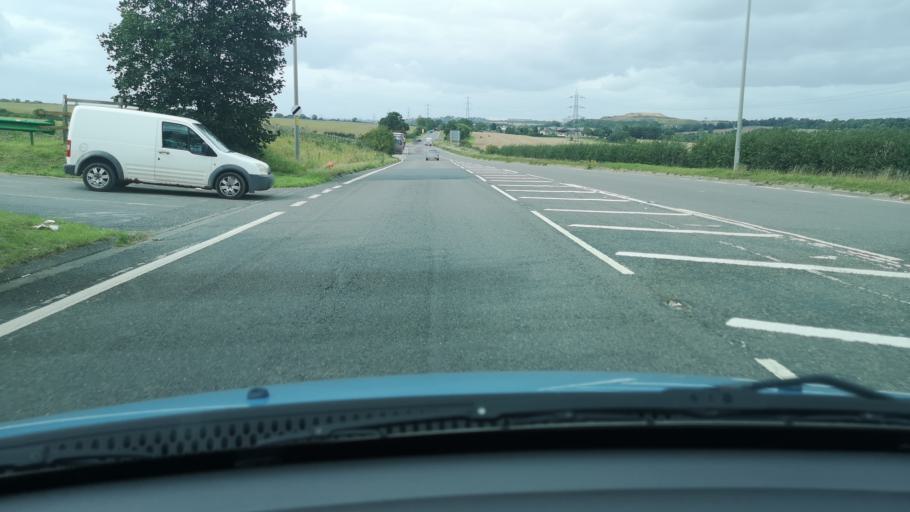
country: GB
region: England
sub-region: Doncaster
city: Marr
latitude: 53.5814
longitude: -1.2247
